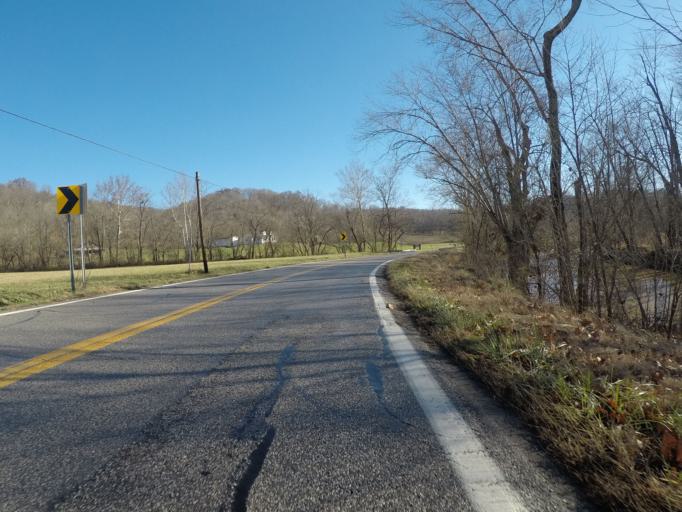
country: US
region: West Virginia
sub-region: Cabell County
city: Huntington
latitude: 38.4855
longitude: -82.4530
